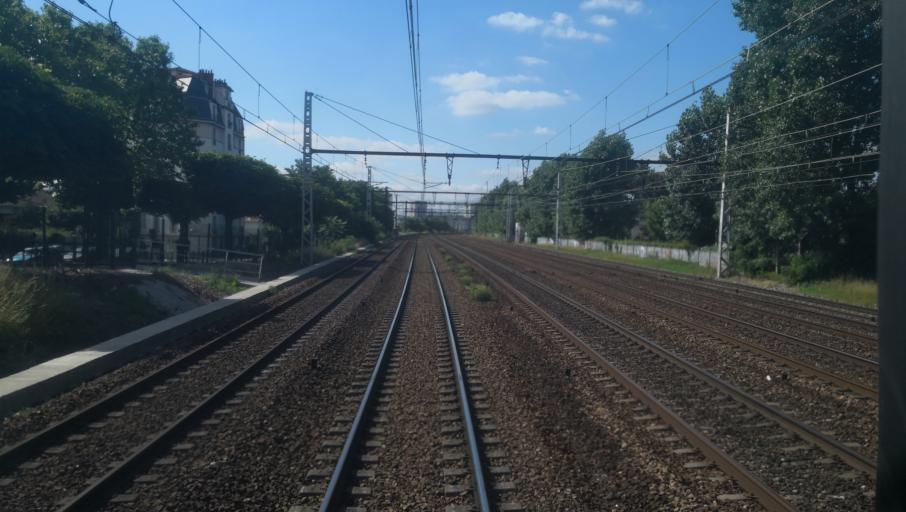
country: FR
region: Ile-de-France
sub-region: Departement du Val-de-Marne
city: Alfortville
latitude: 48.8103
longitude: 2.4218
